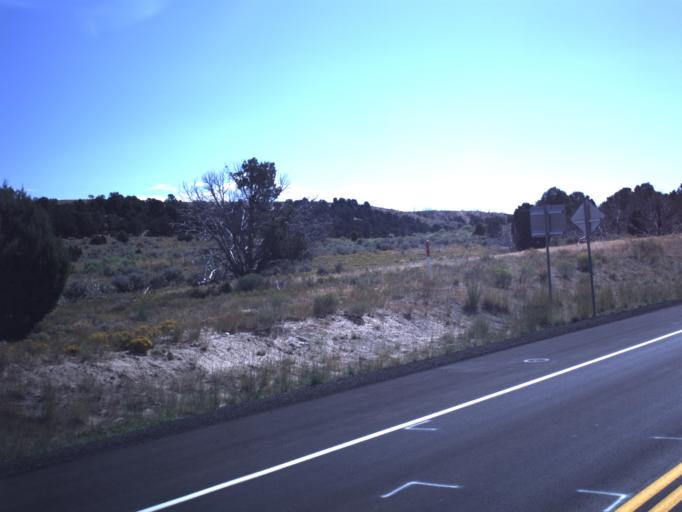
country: US
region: Utah
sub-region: Utah County
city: Genola
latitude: 39.9577
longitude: -112.2439
